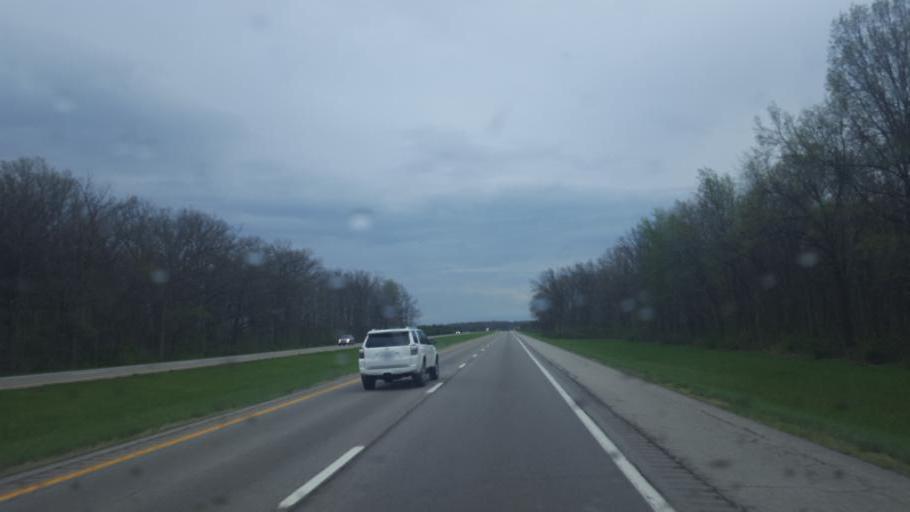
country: US
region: Ohio
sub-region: Wyandot County
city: Carey
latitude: 40.9300
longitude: -83.3757
